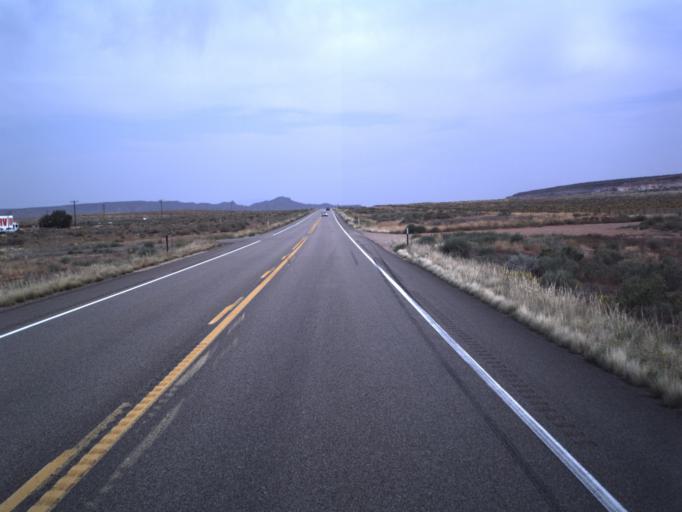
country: US
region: Arizona
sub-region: Coconino County
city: Page
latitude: 37.0971
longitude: -111.7747
